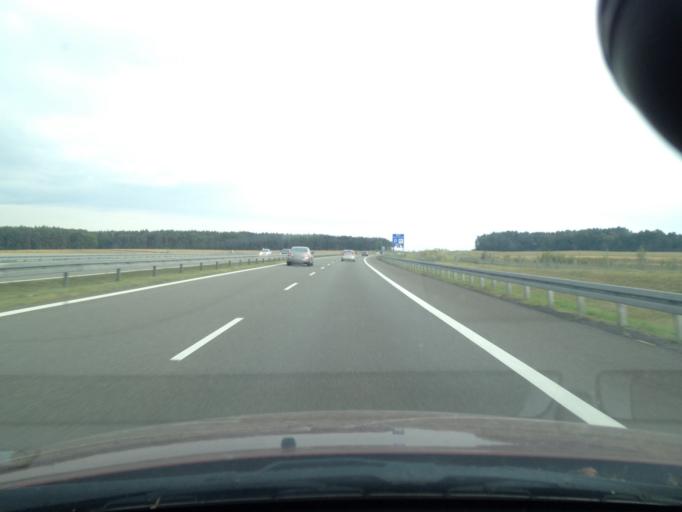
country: PL
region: Lubusz
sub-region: Powiat zielonogorski
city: Sulechow
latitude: 52.1244
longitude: 15.5764
